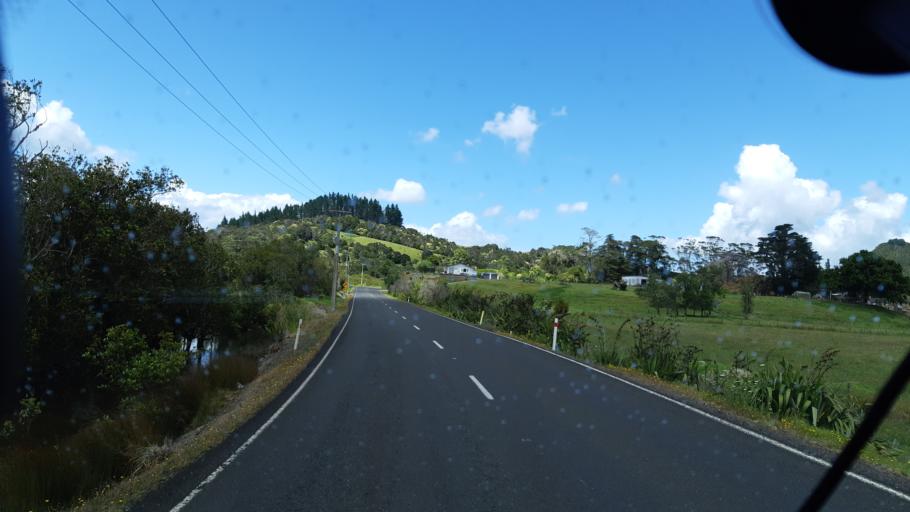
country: NZ
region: Northland
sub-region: Far North District
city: Taipa
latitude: -35.2721
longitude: 173.5221
